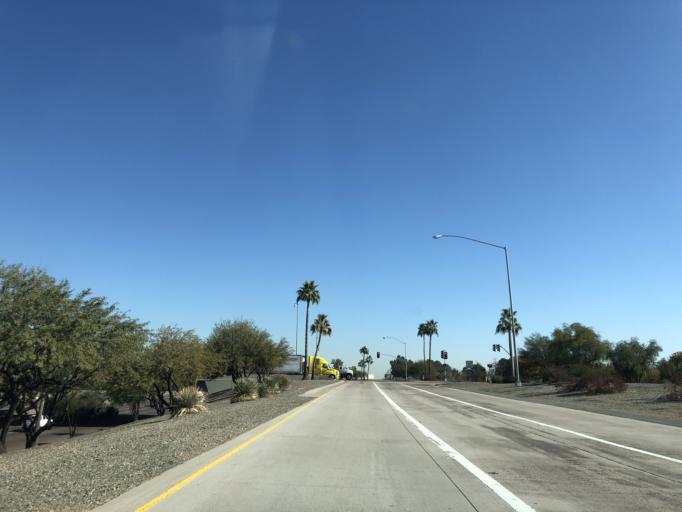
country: US
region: Arizona
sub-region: Maricopa County
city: Tolleson
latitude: 33.4616
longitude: -112.2565
